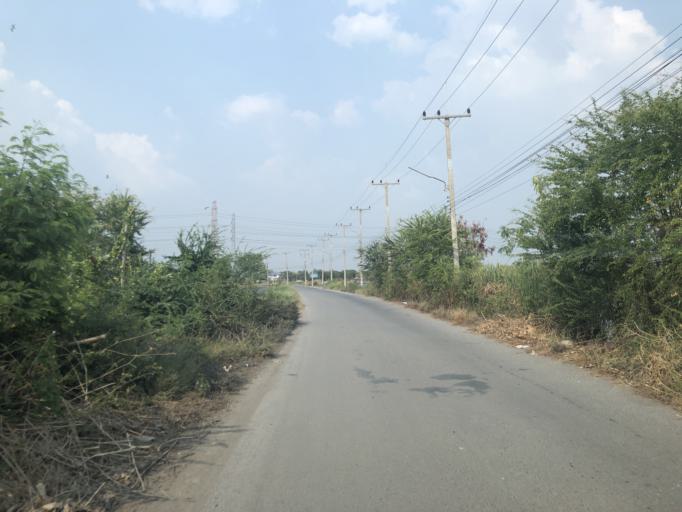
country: TH
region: Chachoengsao
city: Bang Pakong
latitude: 13.5178
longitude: 100.9390
